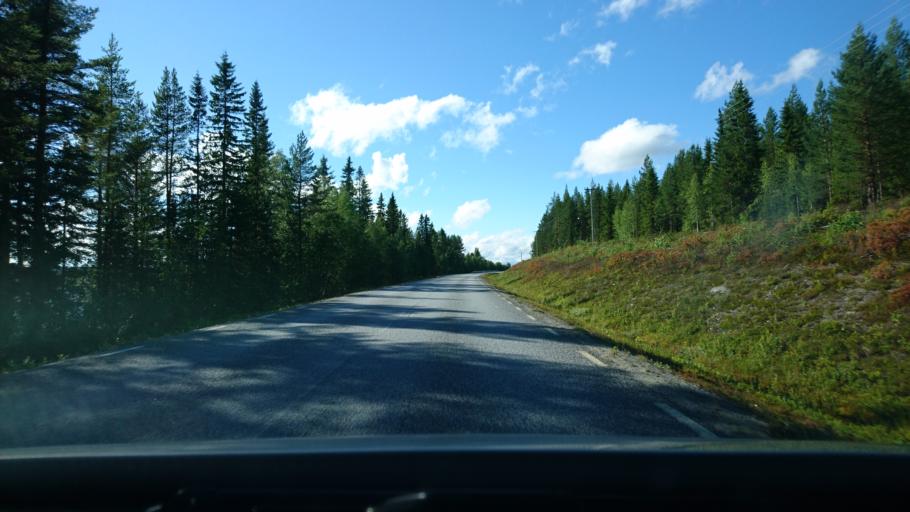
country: SE
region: Vaesterbotten
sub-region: Vilhelmina Kommun
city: Vilhelmina
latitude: 64.3686
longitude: 16.9219
